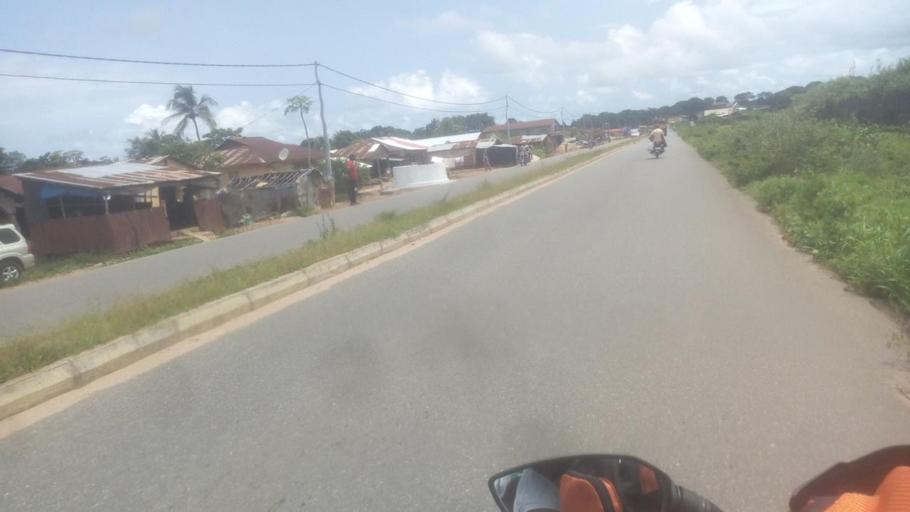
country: SL
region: Northern Province
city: Masoyila
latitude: 8.6127
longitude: -13.1923
